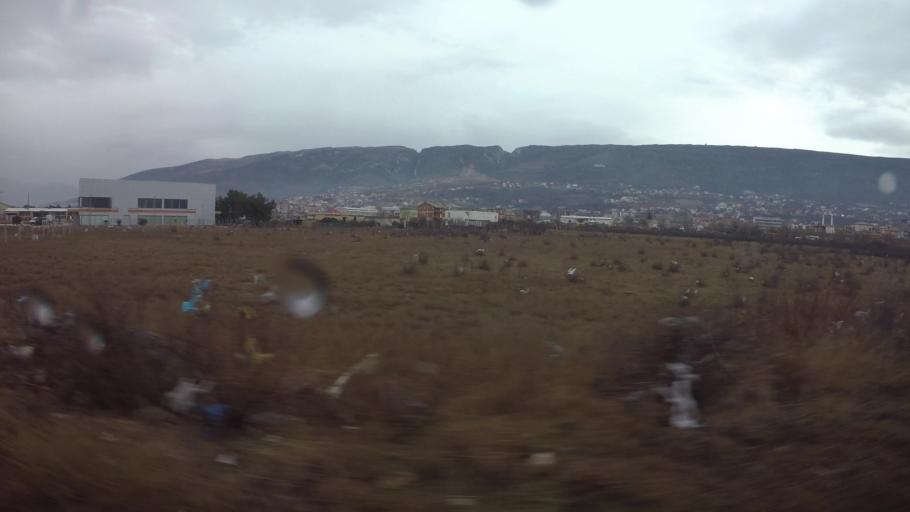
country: BA
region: Federation of Bosnia and Herzegovina
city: Rodoc
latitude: 43.3026
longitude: 17.8343
